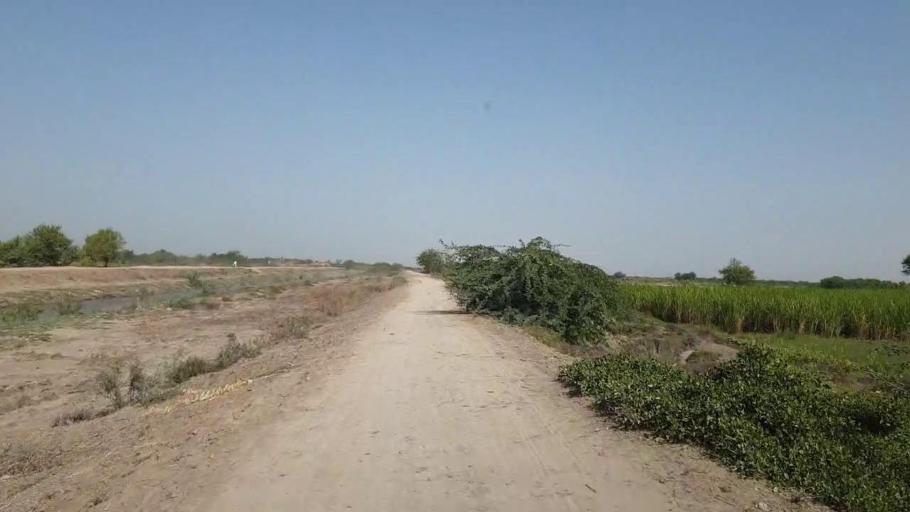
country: PK
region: Sindh
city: Kadhan
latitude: 24.6401
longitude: 69.0724
